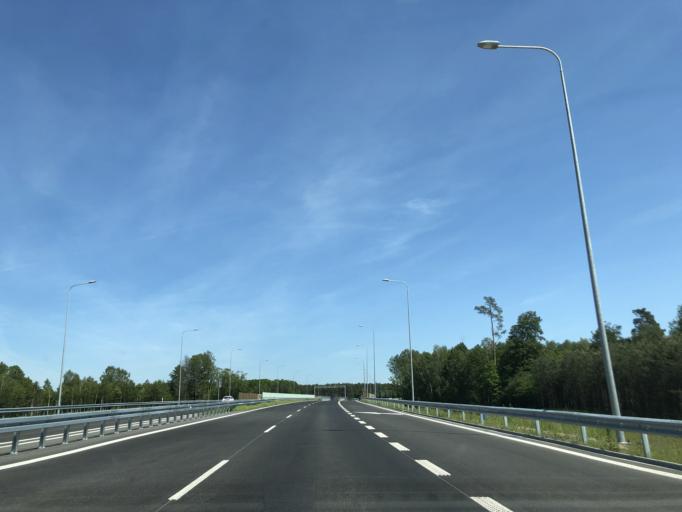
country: PL
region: West Pomeranian Voivodeship
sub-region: Powiat goleniowski
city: Osina
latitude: 53.6336
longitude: 14.9972
